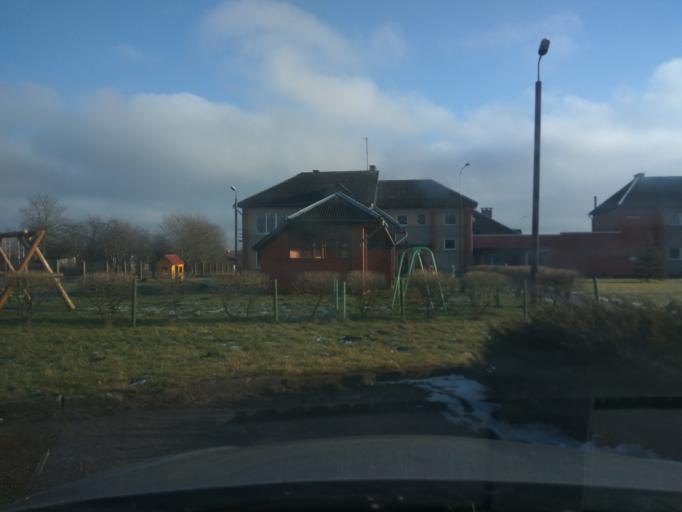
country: LV
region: Broceni
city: Broceni
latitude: 56.8277
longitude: 22.4052
